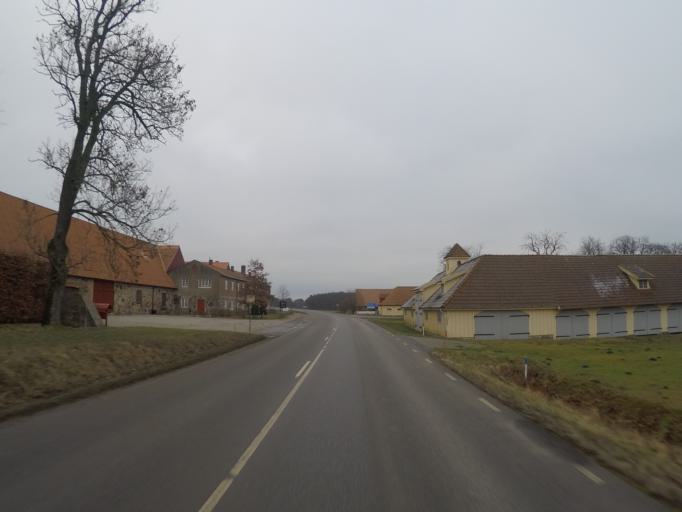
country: SE
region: Skane
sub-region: Hoors Kommun
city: Loberod
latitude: 55.7717
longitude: 13.4823
